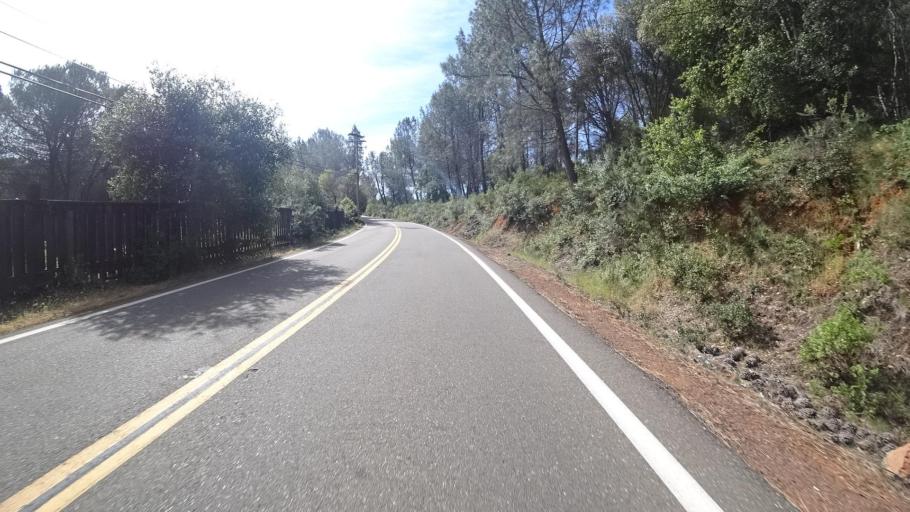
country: US
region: California
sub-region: Lake County
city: Soda Bay
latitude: 38.9870
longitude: -122.7441
